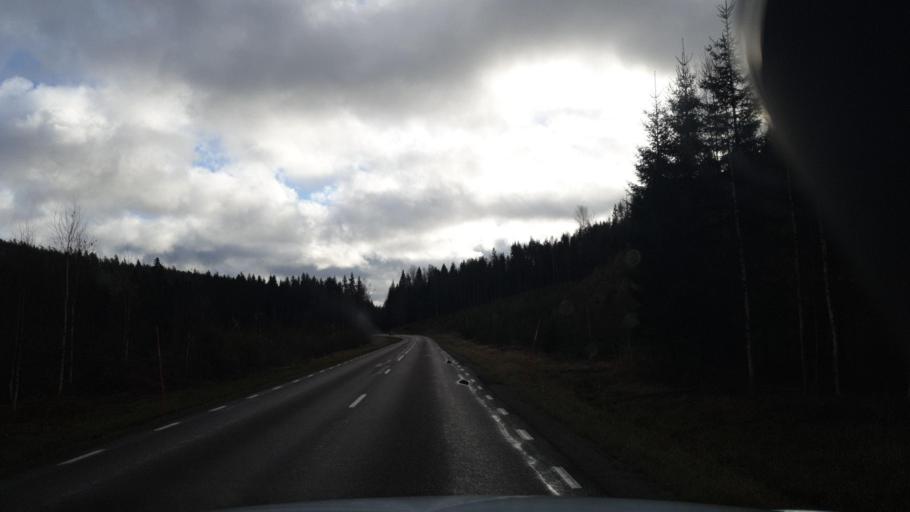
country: SE
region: Vaermland
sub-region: Arvika Kommun
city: Arvika
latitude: 59.4684
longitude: 12.8226
